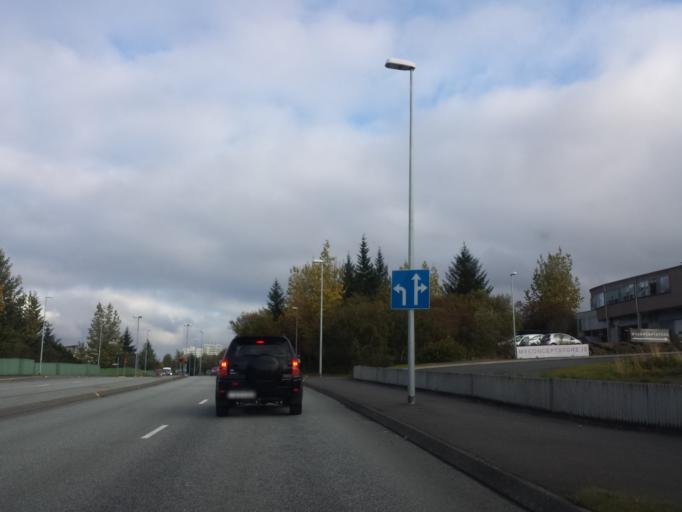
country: IS
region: Capital Region
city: Reykjavik
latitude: 64.1142
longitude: -21.8890
